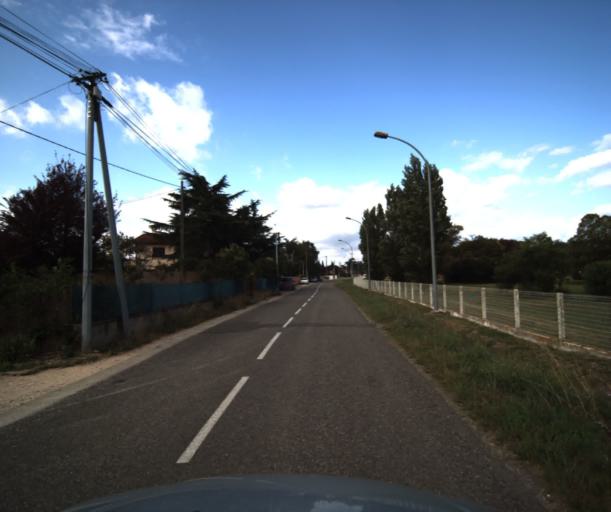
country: FR
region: Midi-Pyrenees
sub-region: Departement de la Haute-Garonne
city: Muret
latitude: 43.4434
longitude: 1.3097
